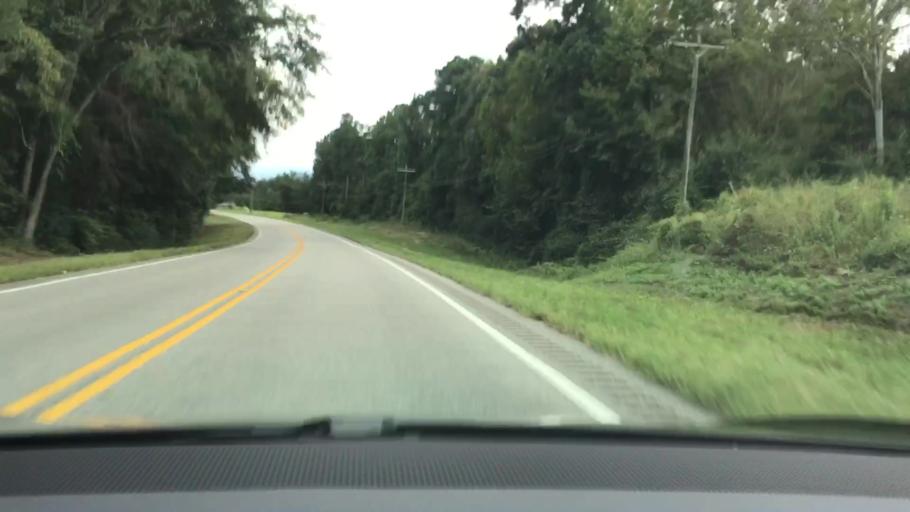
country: US
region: Alabama
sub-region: Coffee County
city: Elba
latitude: 31.5947
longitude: -86.0056
